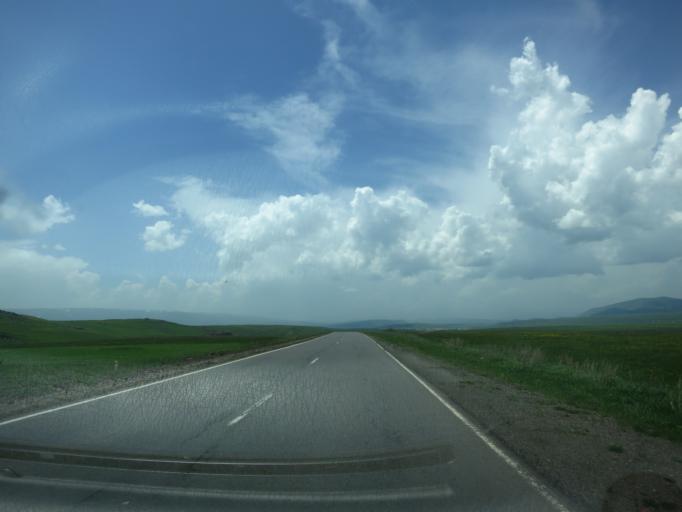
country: GE
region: Samtskhe-Javakheti
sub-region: Ninotsminda
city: Ninotsminda
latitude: 41.2921
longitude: 43.7056
